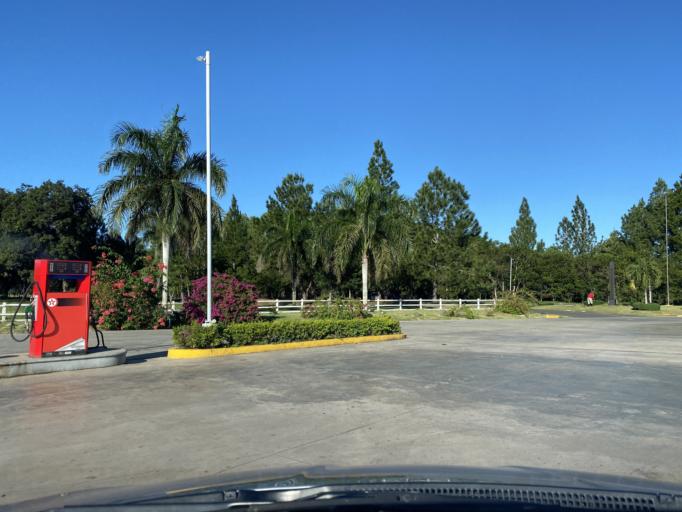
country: DO
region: Monte Plata
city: Monte Plata
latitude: 18.7686
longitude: -69.7537
